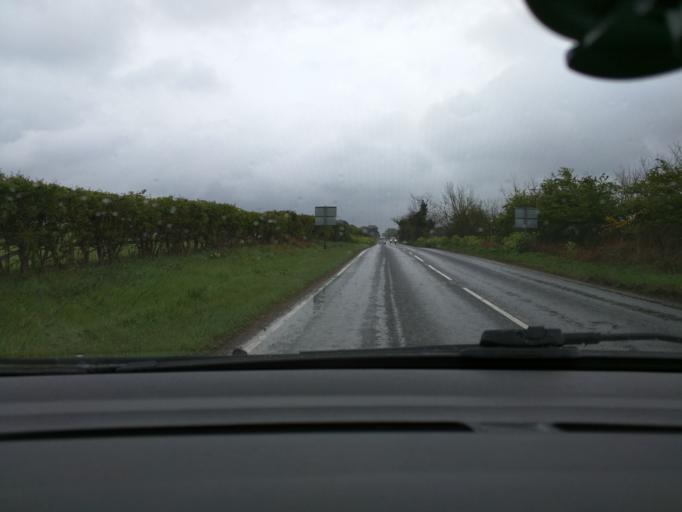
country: GB
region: England
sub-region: Suffolk
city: Saxmundham
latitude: 52.1799
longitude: 1.5063
